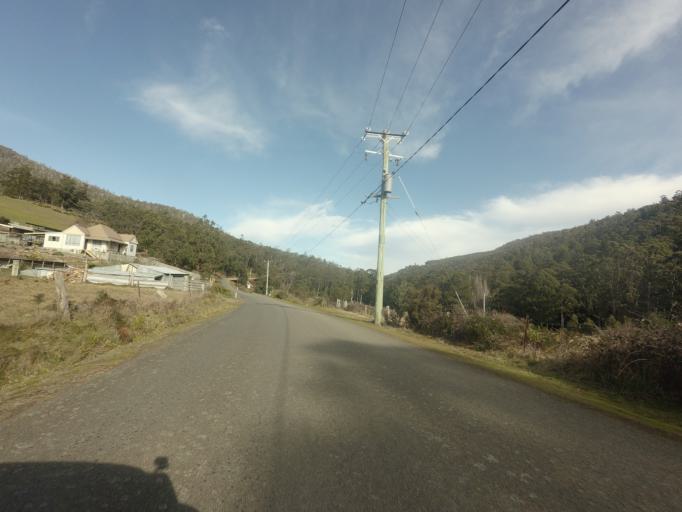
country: AU
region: Tasmania
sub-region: Huon Valley
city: Huonville
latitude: -43.0506
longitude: 147.1076
